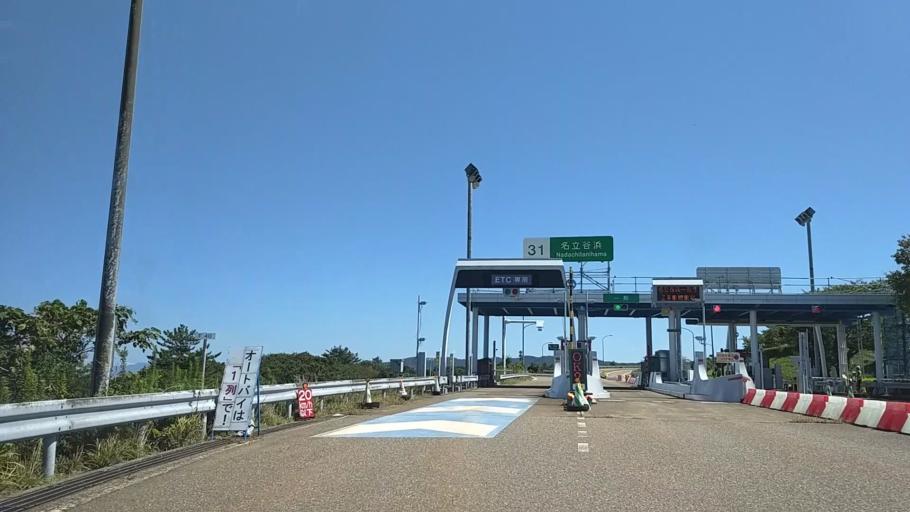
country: JP
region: Niigata
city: Joetsu
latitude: 37.1689
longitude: 138.1108
